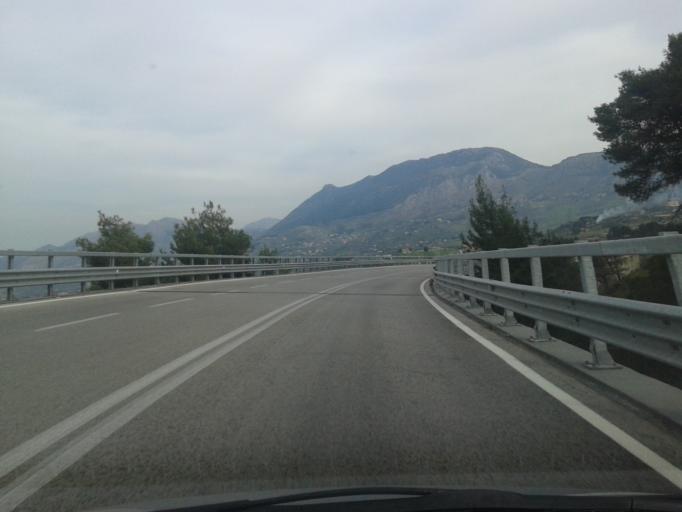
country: IT
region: Sicily
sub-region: Palermo
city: Giacalone
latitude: 38.0379
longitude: 13.2385
